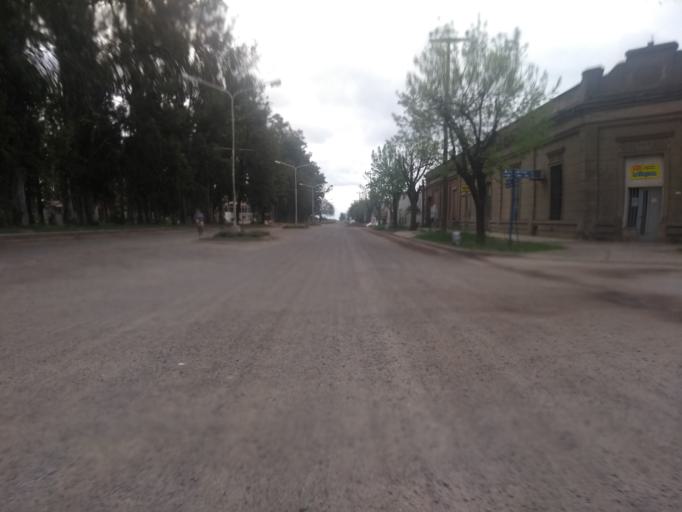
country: AR
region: Santa Fe
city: Galvez
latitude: -31.9060
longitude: -61.2804
